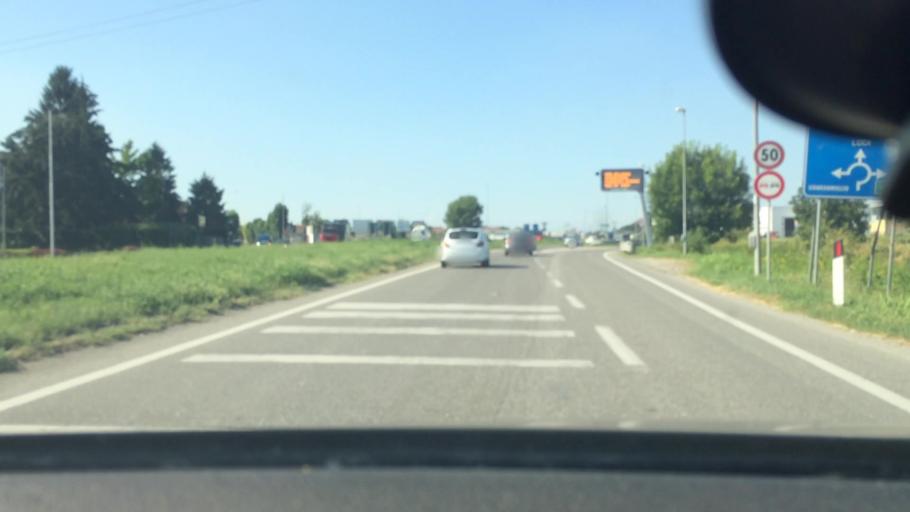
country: IT
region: Lombardy
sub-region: Provincia di Lodi
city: Guardamiglio
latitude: 45.1045
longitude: 9.6848
